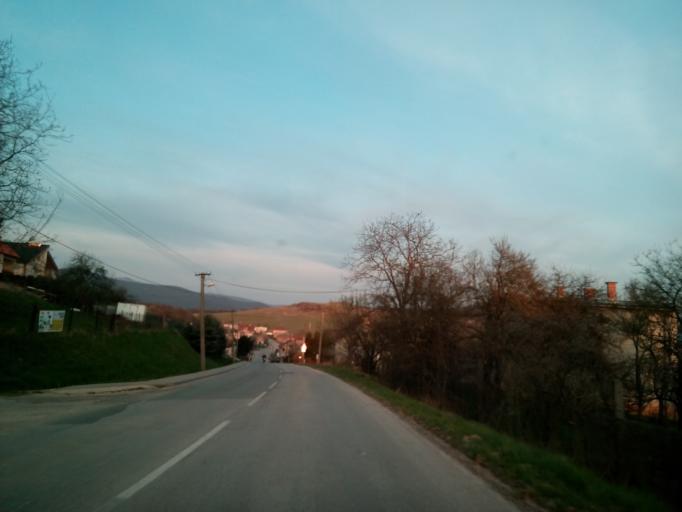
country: SK
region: Kosicky
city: Roznava
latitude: 48.6596
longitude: 20.4850
